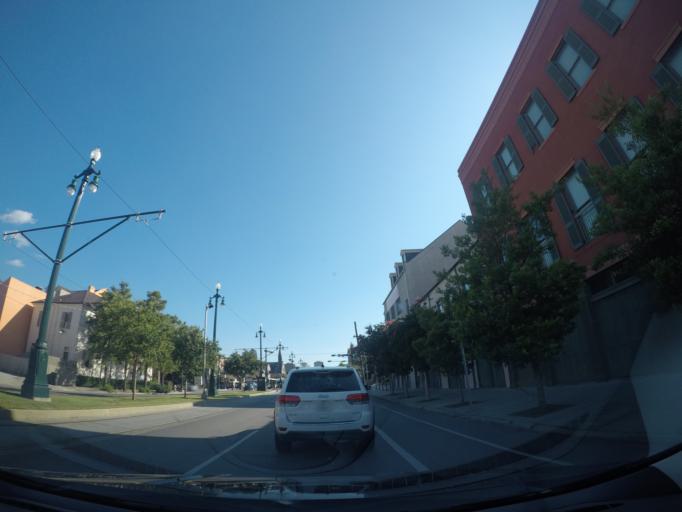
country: US
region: Louisiana
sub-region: Orleans Parish
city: New Orleans
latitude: 29.9665
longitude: -90.0633
